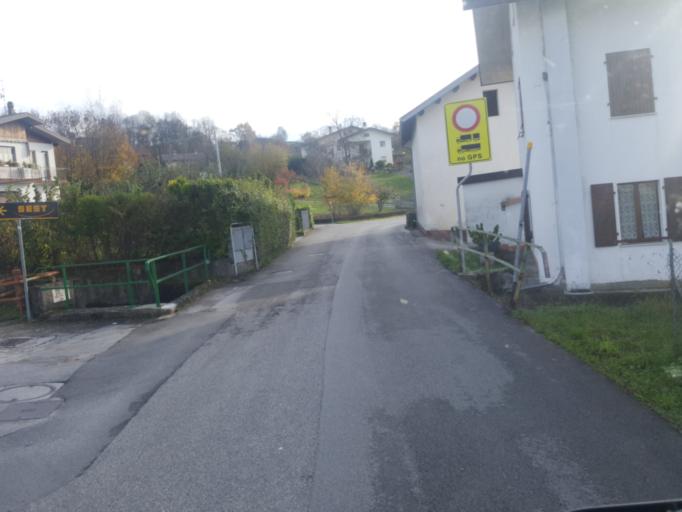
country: IT
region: Veneto
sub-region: Provincia di Belluno
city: Limana
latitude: 46.0948
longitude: 12.1819
